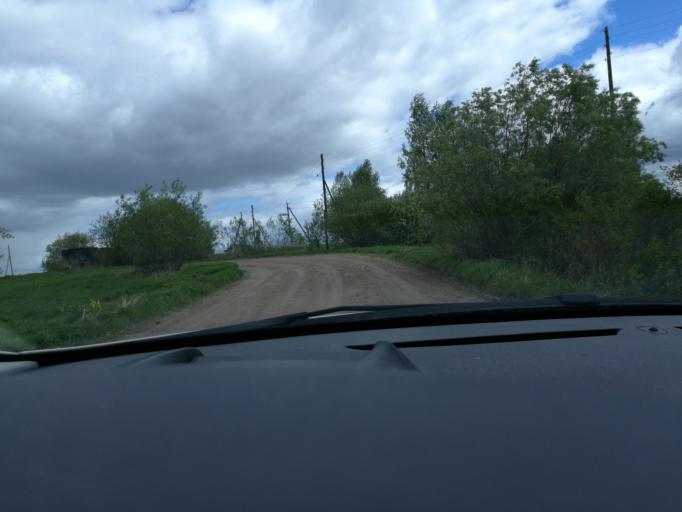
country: RU
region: Arkhangelskaya
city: Lukovetskiy
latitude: 64.2530
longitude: 41.7914
